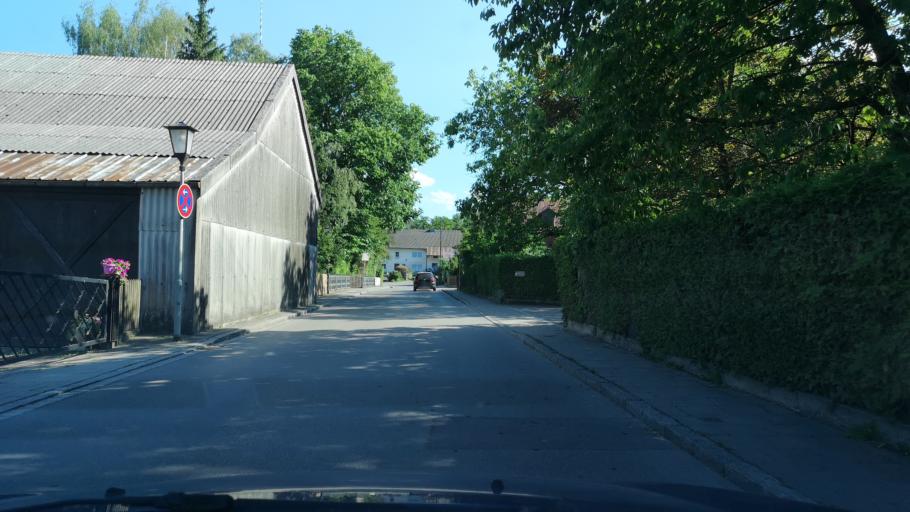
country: DE
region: Bavaria
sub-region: Upper Bavaria
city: Eichenried
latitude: 48.2474
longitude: 11.7793
